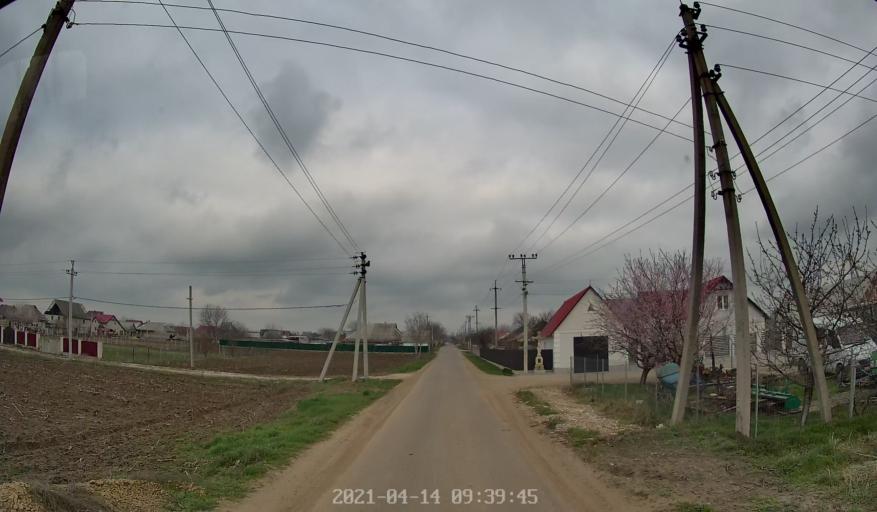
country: MD
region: Chisinau
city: Vadul lui Voda
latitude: 47.1330
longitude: 29.1262
